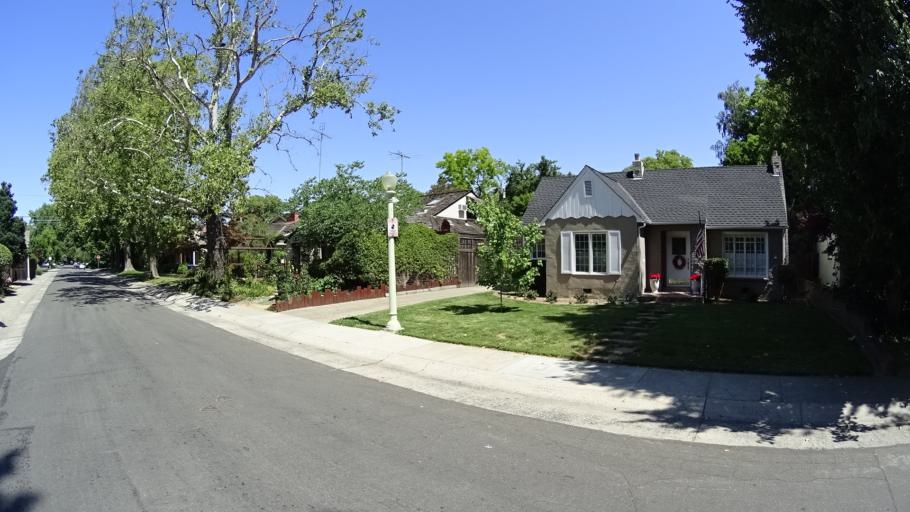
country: US
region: California
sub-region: Sacramento County
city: Sacramento
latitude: 38.5550
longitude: -121.4928
